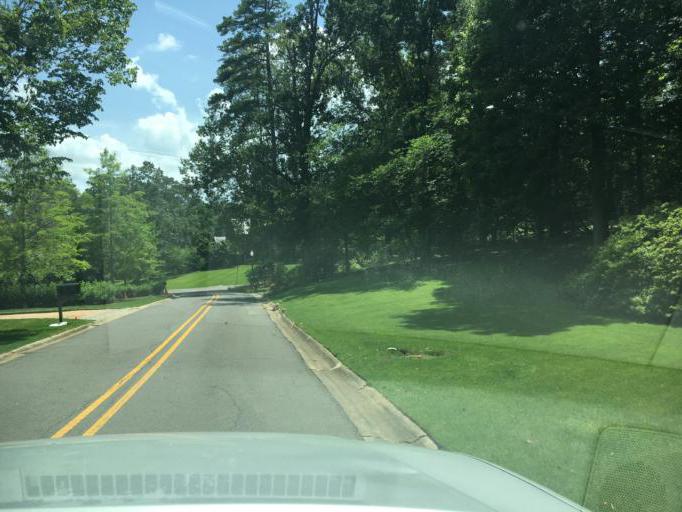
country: US
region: Alabama
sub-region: Jefferson County
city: Mountain Brook
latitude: 33.4824
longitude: -86.7630
